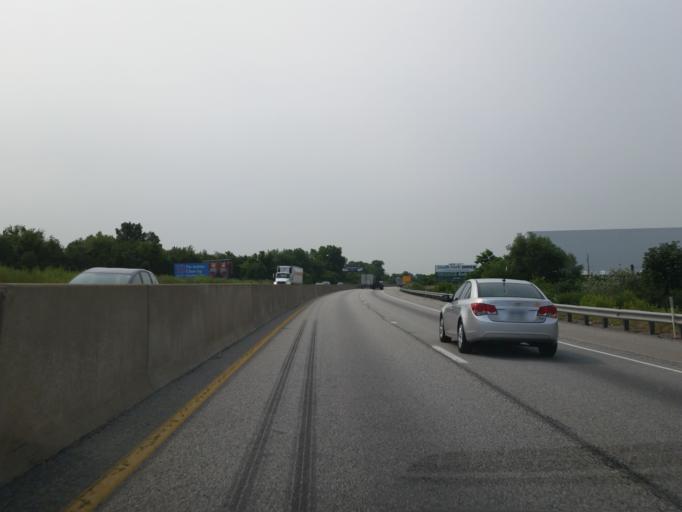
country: US
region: Pennsylvania
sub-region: York County
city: Manchester
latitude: 40.0730
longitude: -76.7595
